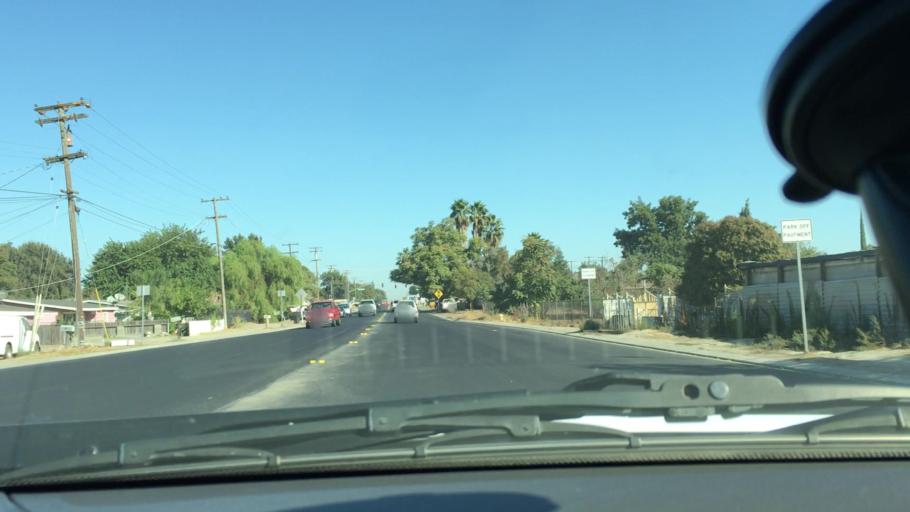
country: US
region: California
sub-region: Stanislaus County
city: West Modesto
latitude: 37.6137
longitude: -121.0304
